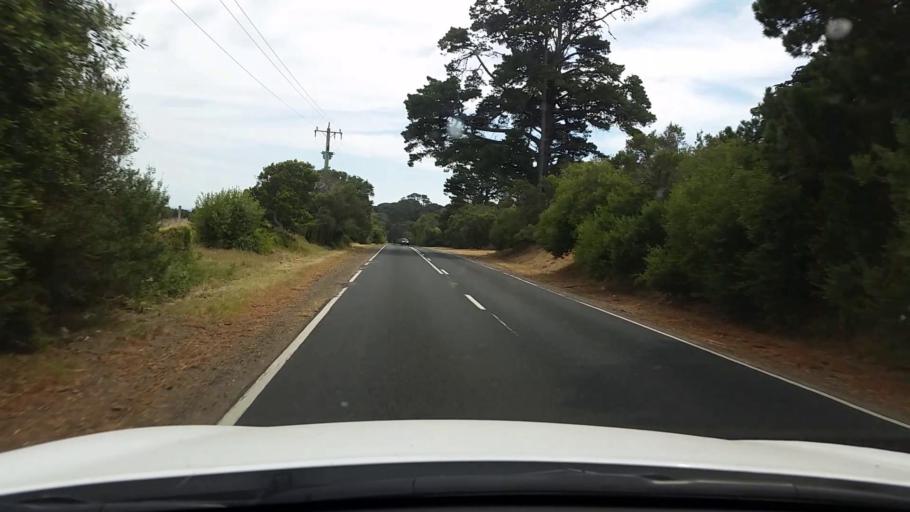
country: AU
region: Victoria
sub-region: Mornington Peninsula
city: Saint Andrews Beach
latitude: -38.4390
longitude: 144.8968
